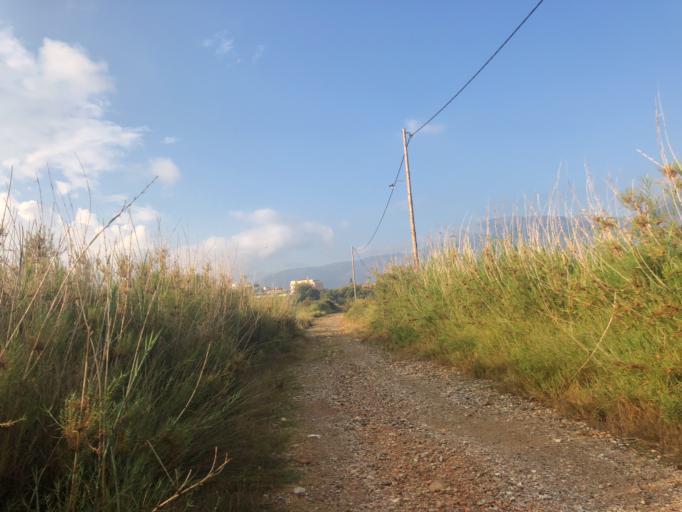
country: GR
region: Crete
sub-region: Nomos Chanias
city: Georgioupolis
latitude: 35.3523
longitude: 24.3088
